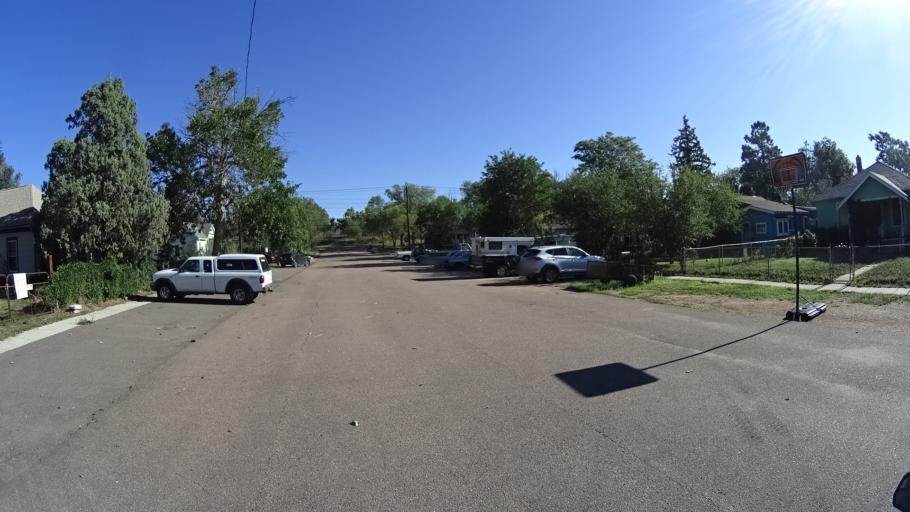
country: US
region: Colorado
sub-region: El Paso County
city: Colorado Springs
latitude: 38.8194
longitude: -104.8279
